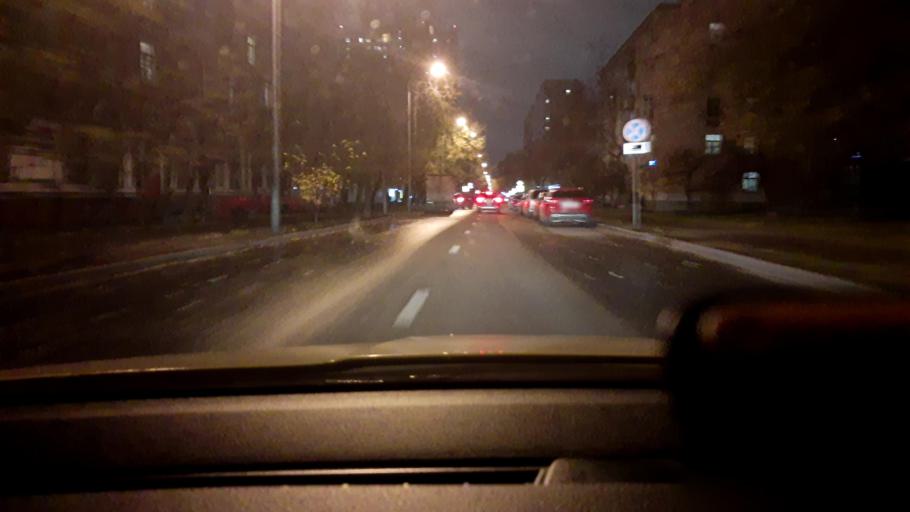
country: RU
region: Moscow
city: Novyye Kuz'minki
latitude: 55.6974
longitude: 37.7499
